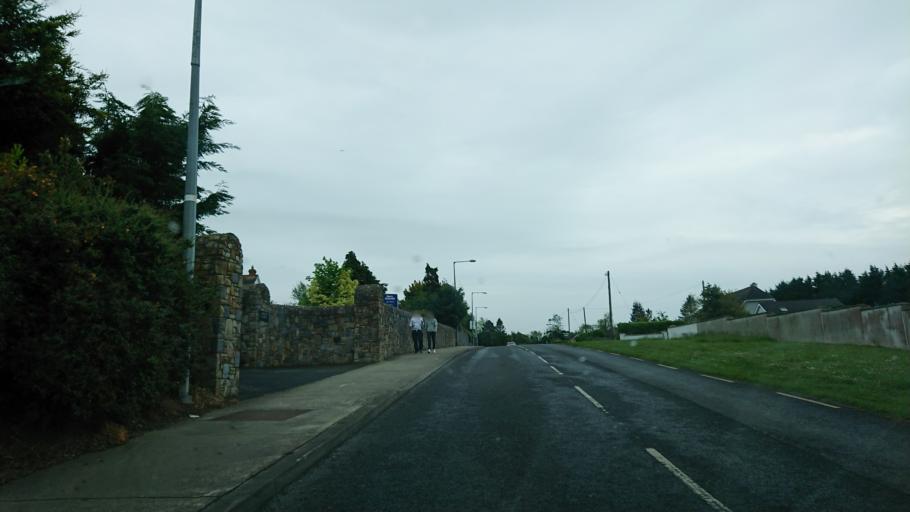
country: IE
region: Munster
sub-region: Waterford
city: Waterford
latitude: 52.2377
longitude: -7.0829
